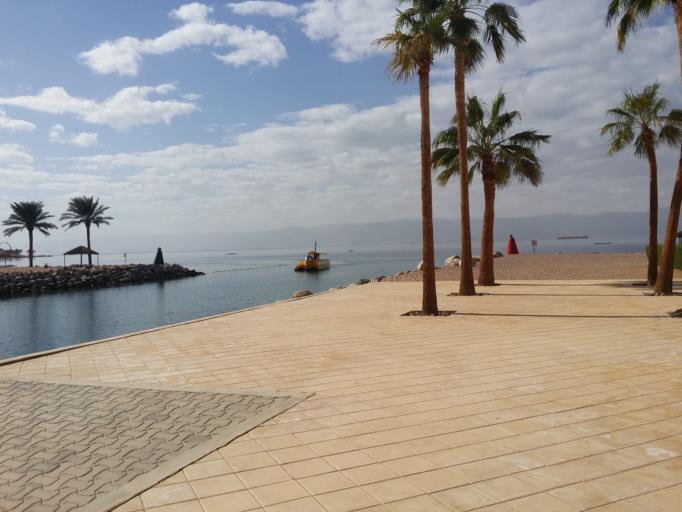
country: JO
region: Aqaba
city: Aqaba
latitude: 29.4091
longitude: 34.9785
